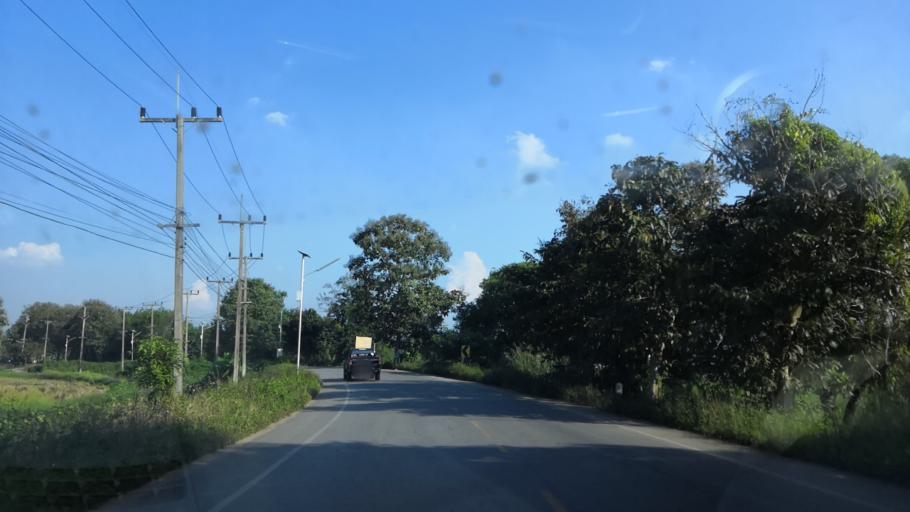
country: TH
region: Chiang Rai
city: Chiang Rai
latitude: 19.9326
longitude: 99.8865
